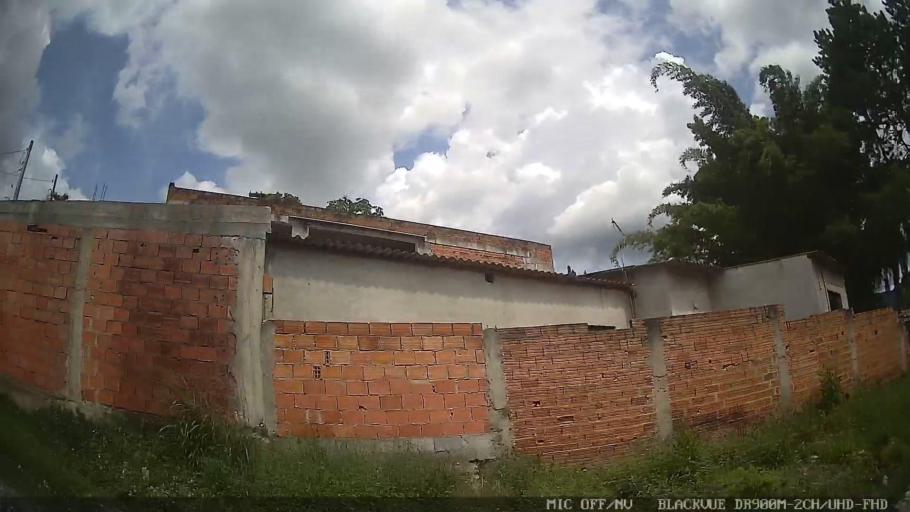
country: BR
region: Sao Paulo
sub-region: Rio Grande Da Serra
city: Rio Grande da Serra
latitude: -23.6962
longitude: -46.2363
